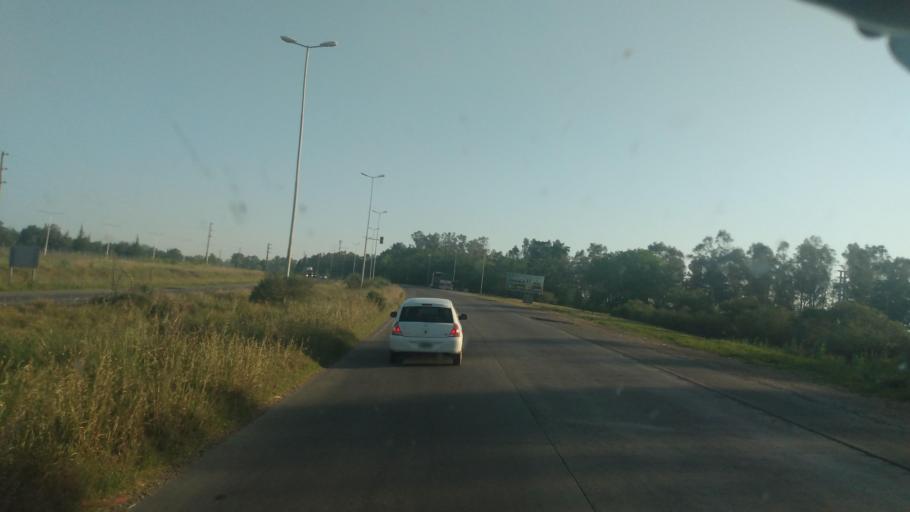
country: AR
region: Buenos Aires
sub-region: Partido de Campana
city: Campana
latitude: -34.2428
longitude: -58.9660
